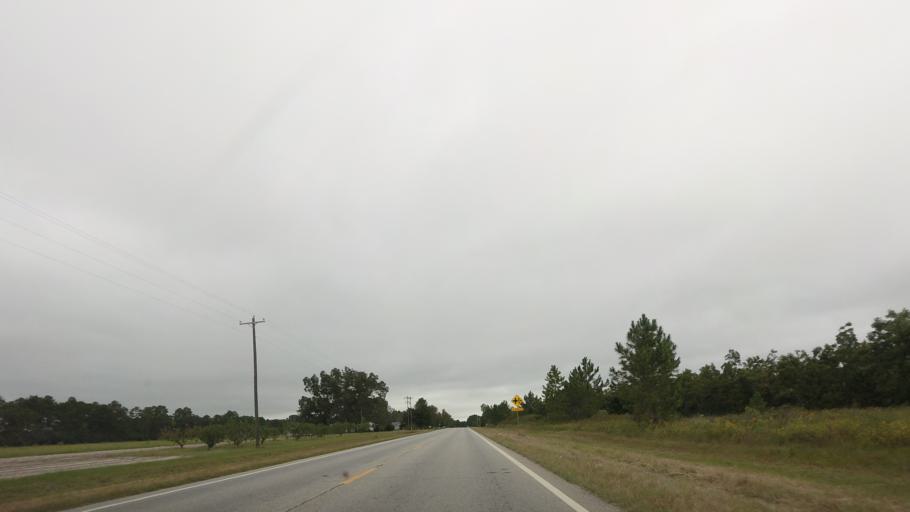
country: US
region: Georgia
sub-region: Berrien County
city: Ray City
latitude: 31.1268
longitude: -83.2138
